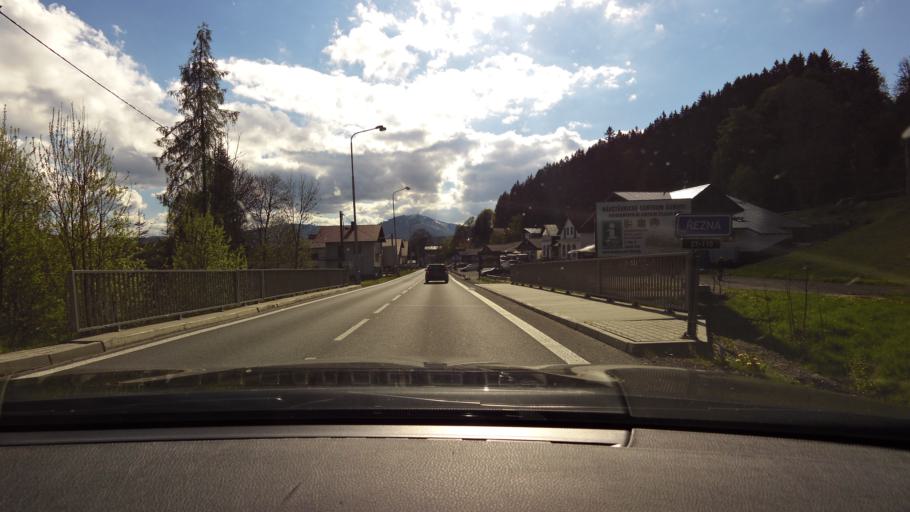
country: CZ
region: Plzensky
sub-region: Okres Klatovy
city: Zelezna Ruda
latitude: 49.1398
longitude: 13.2424
